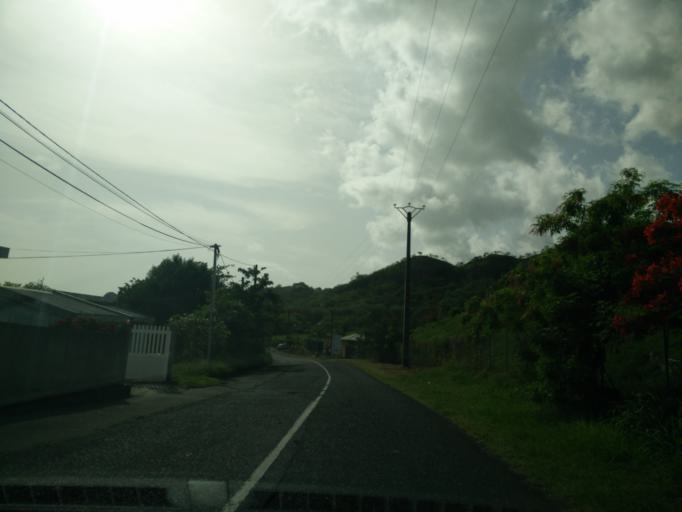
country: MQ
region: Martinique
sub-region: Martinique
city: Saint-Pierre
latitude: 14.7805
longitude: -61.2044
